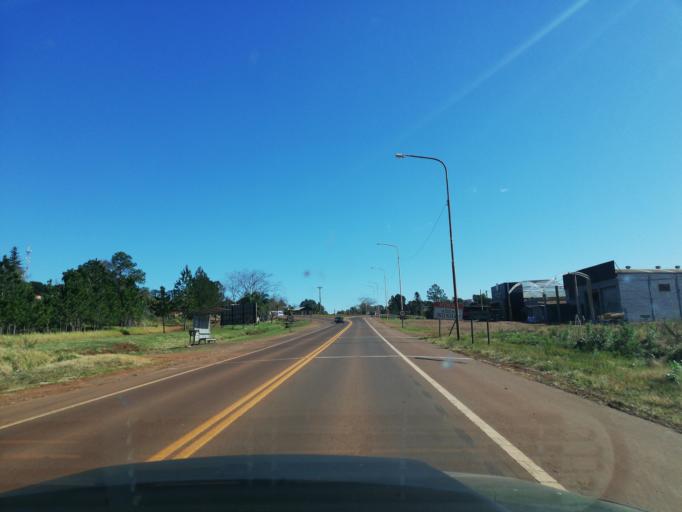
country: AR
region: Misiones
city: Aristobulo del Valle
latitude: -27.1004
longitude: -54.8824
